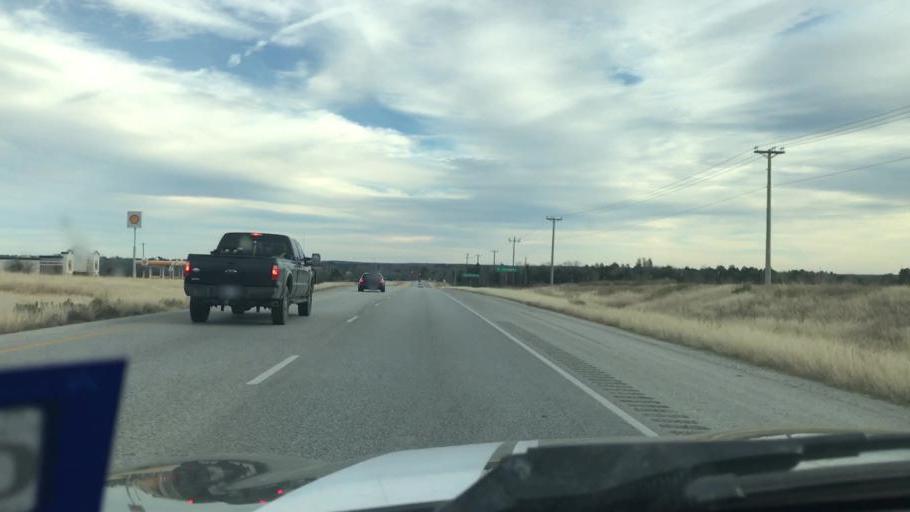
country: US
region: Texas
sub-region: Bastrop County
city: Elgin
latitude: 30.3125
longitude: -97.3077
